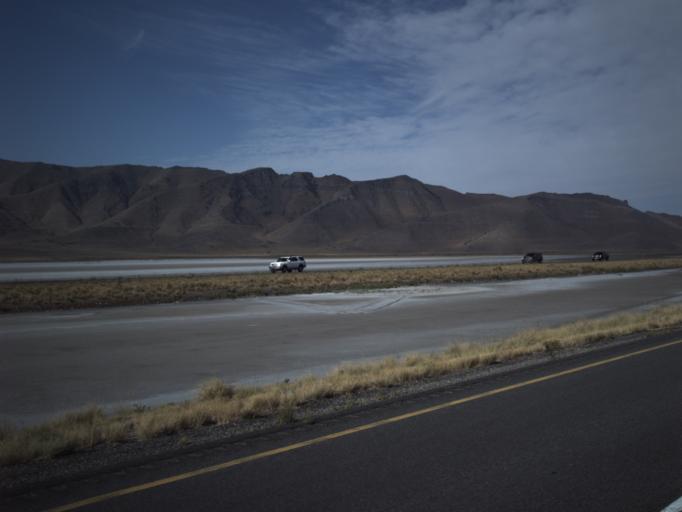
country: US
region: Utah
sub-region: Tooele County
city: Grantsville
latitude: 40.7191
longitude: -112.5513
